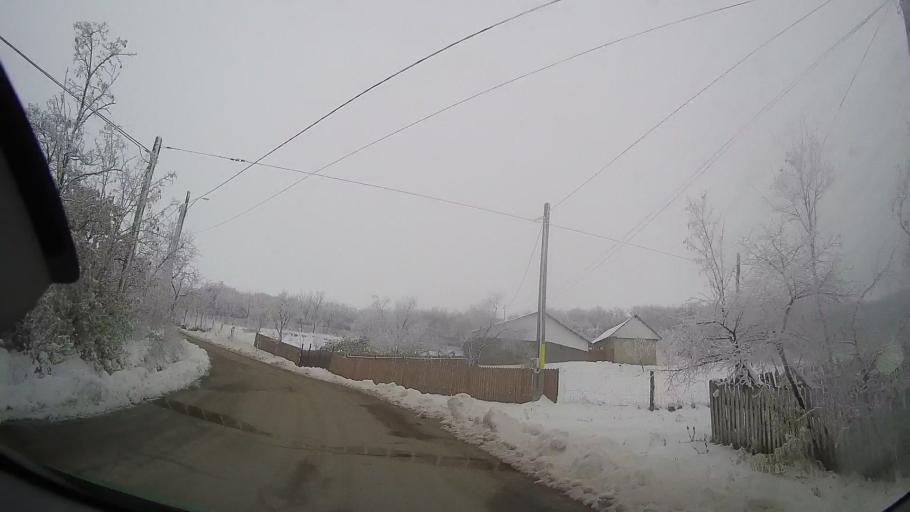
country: RO
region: Iasi
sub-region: Comuna Tibanesti
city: Tibanesti
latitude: 46.8952
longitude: 27.3086
